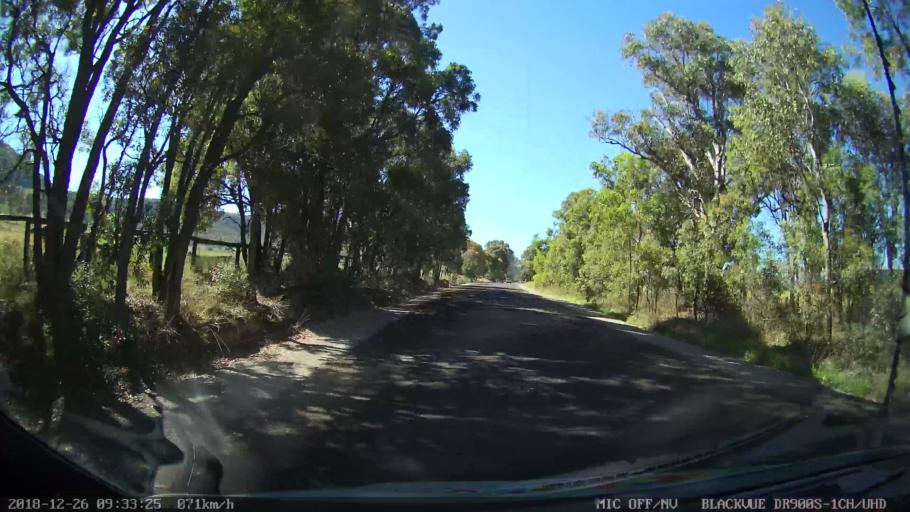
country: AU
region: New South Wales
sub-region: Mid-Western Regional
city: Kandos
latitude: -32.8946
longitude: 150.0349
